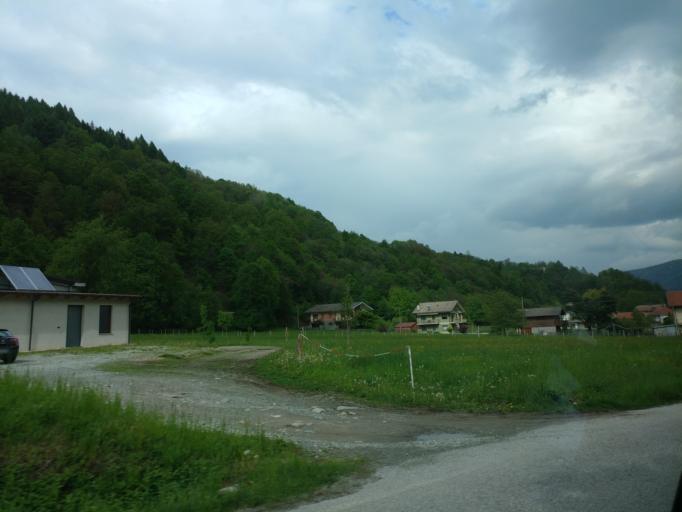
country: IT
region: Piedmont
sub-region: Provincia di Cuneo
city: Paesana
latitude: 44.6866
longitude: 7.2485
